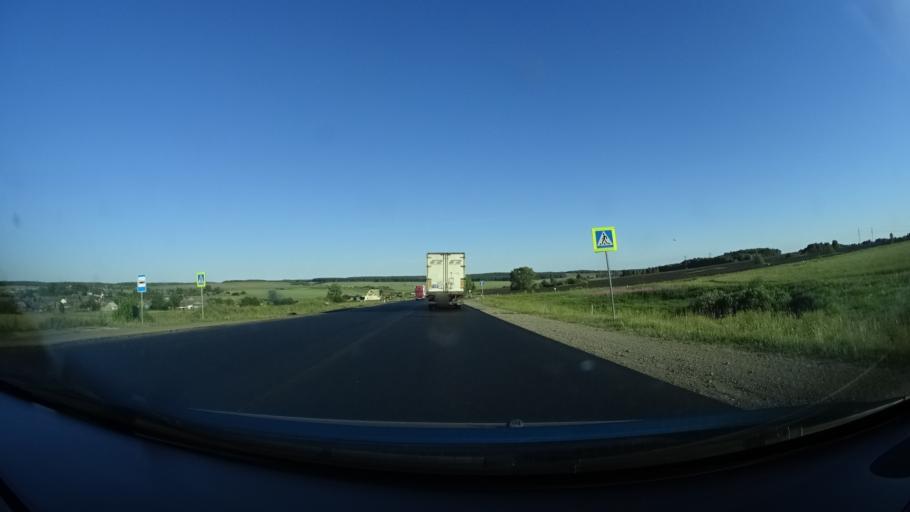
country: RU
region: Sverdlovsk
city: Achit
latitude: 56.8961
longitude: 57.6028
